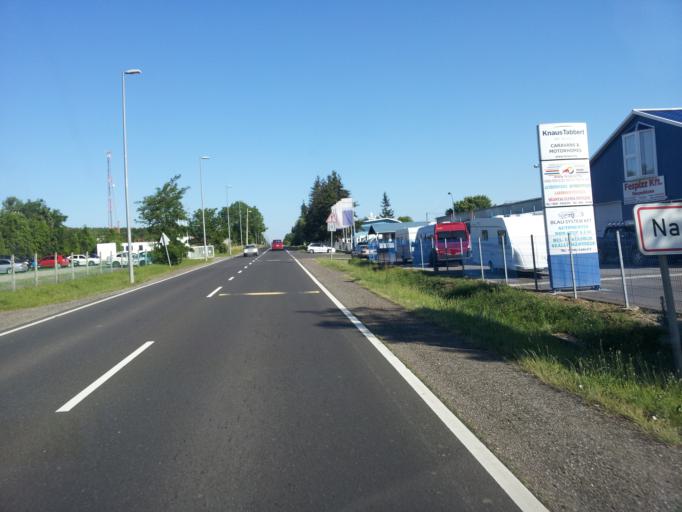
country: HU
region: Nograd
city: Nagyoroszi
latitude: 47.9920
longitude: 19.1042
